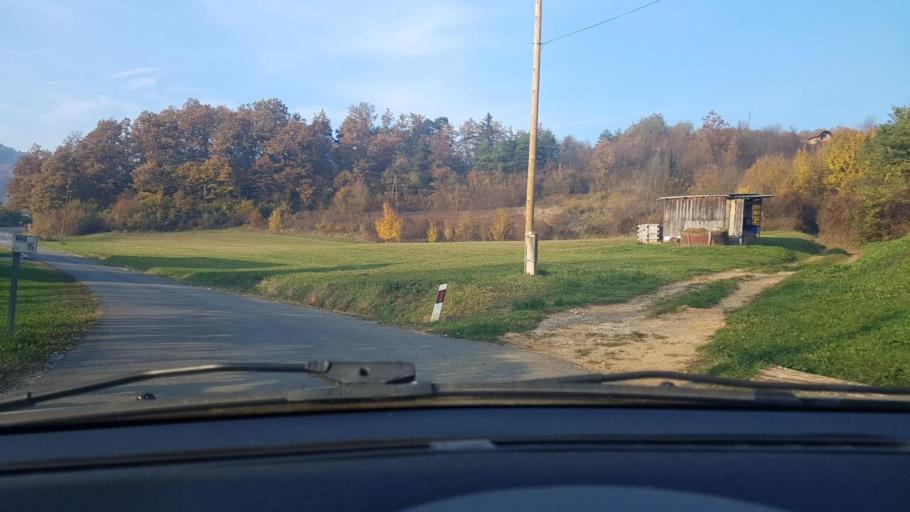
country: SI
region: Podcetrtek
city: Podcetrtek
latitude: 46.1458
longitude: 15.5993
